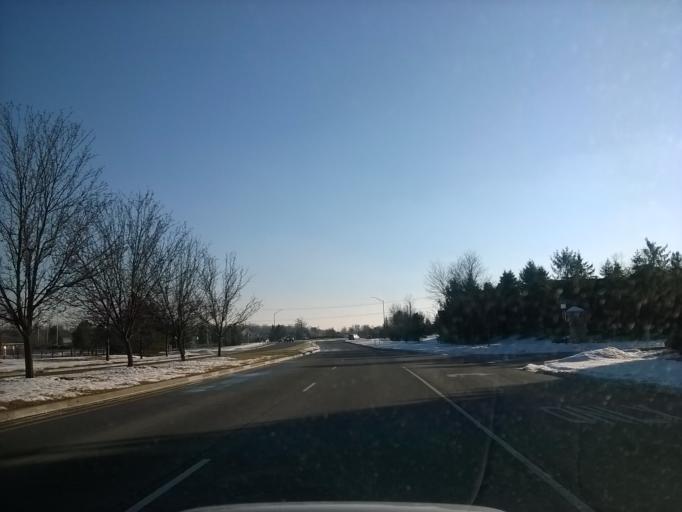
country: US
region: Indiana
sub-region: Hamilton County
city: Carmel
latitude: 39.9731
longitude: -86.0708
